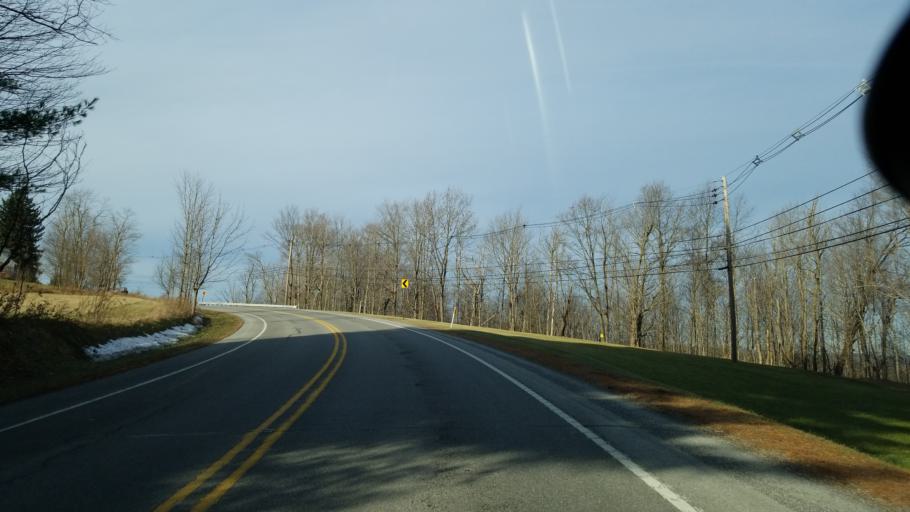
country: US
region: Pennsylvania
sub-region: Clearfield County
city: Curwensville
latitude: 40.9782
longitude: -78.6228
